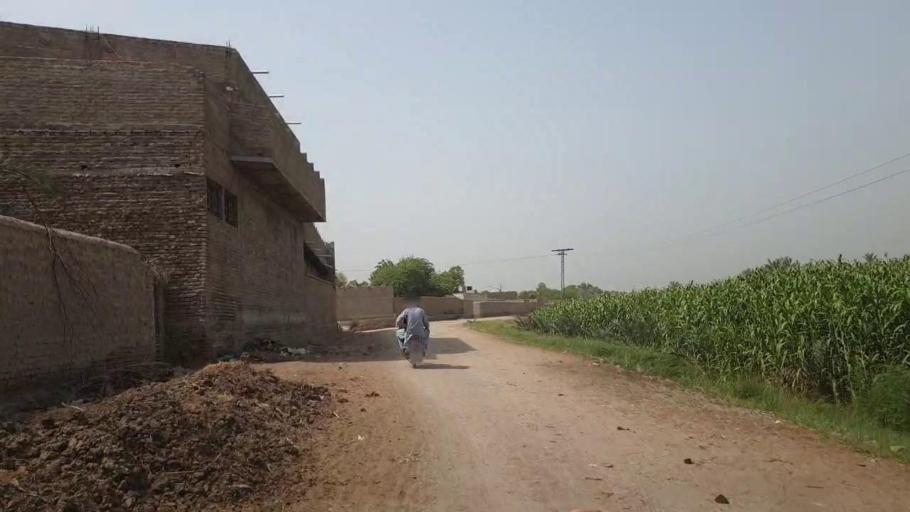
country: PK
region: Sindh
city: Gambat
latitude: 27.4065
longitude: 68.5570
